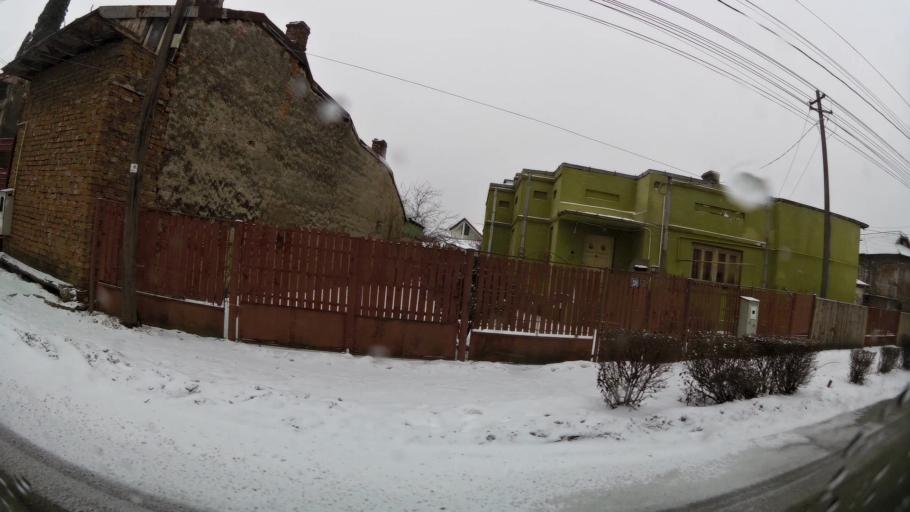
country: RO
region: Dambovita
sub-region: Municipiul Targoviste
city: Targoviste
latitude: 44.9356
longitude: 25.4505
